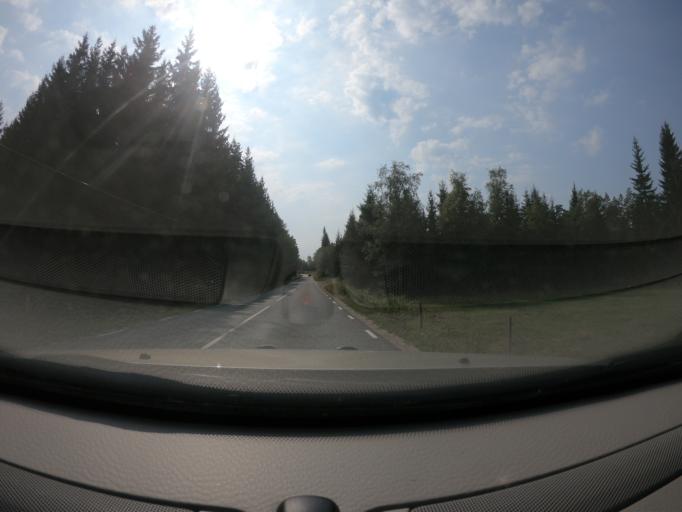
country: SE
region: Joenkoeping
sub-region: Vetlanda Kommun
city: Landsbro
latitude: 57.2984
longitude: 14.8718
